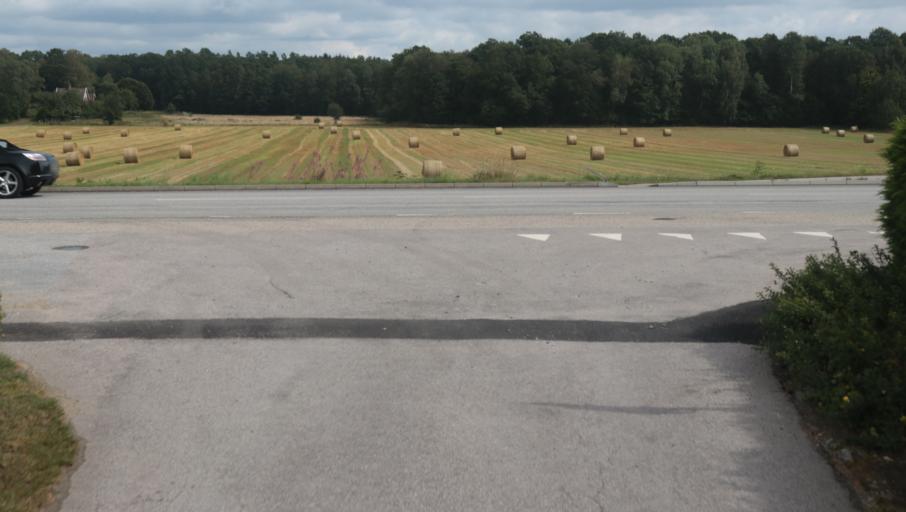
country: SE
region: Blekinge
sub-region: Karlshamns Kommun
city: Karlshamn
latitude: 56.2167
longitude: 14.8327
